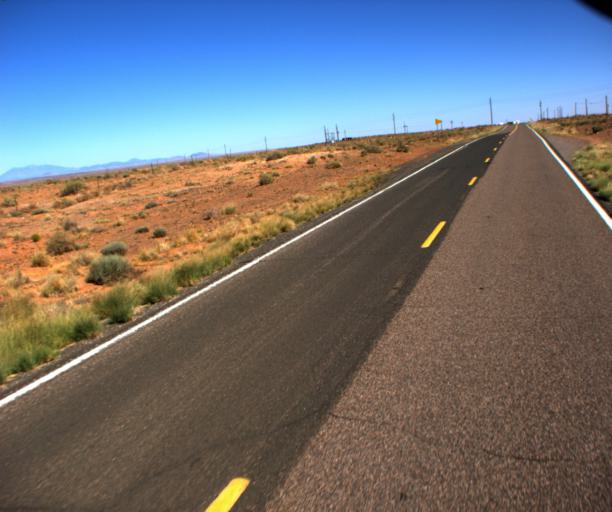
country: US
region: Arizona
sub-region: Coconino County
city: LeChee
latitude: 35.0795
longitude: -110.8604
